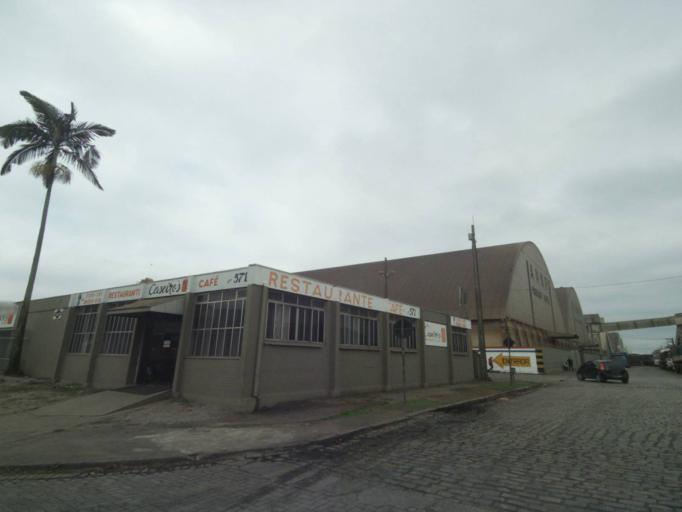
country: BR
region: Parana
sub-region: Paranagua
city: Paranagua
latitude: -25.5085
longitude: -48.5197
